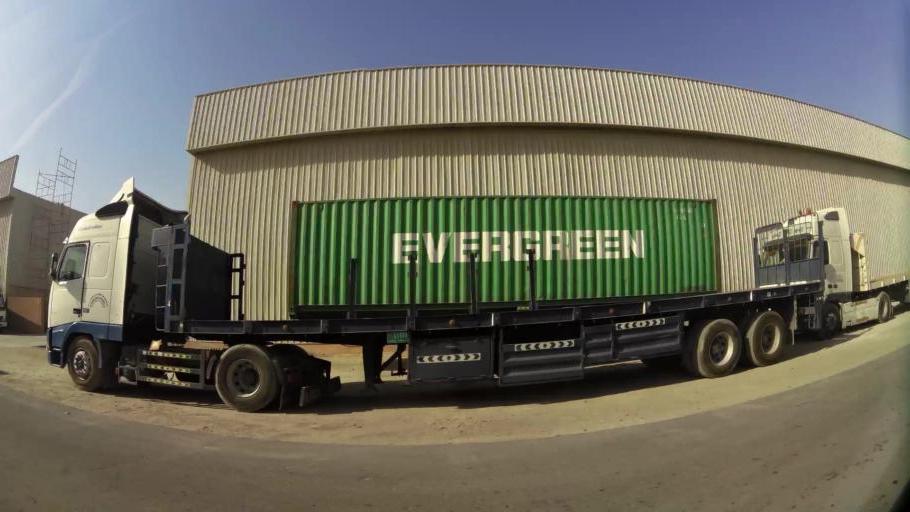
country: AE
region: Ash Shariqah
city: Sharjah
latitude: 25.2828
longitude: 55.3840
